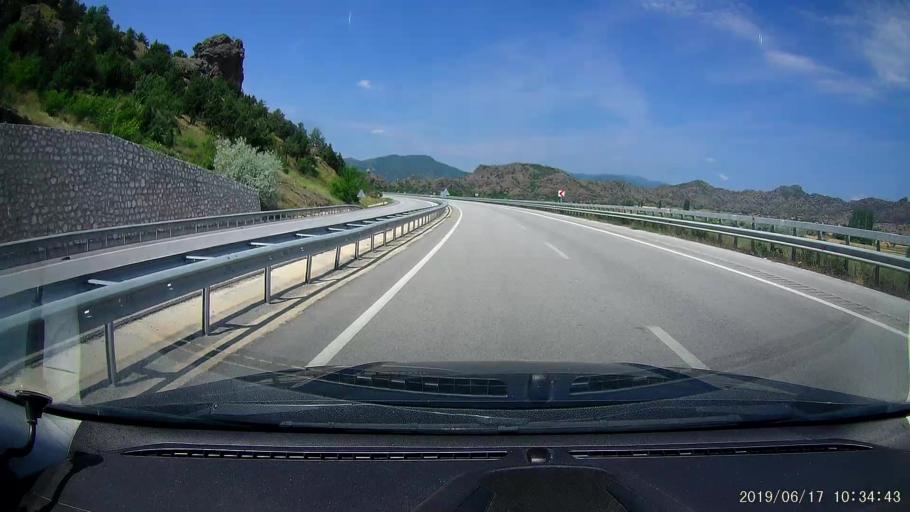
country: TR
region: Corum
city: Osmancik
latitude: 40.9813
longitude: 34.7180
